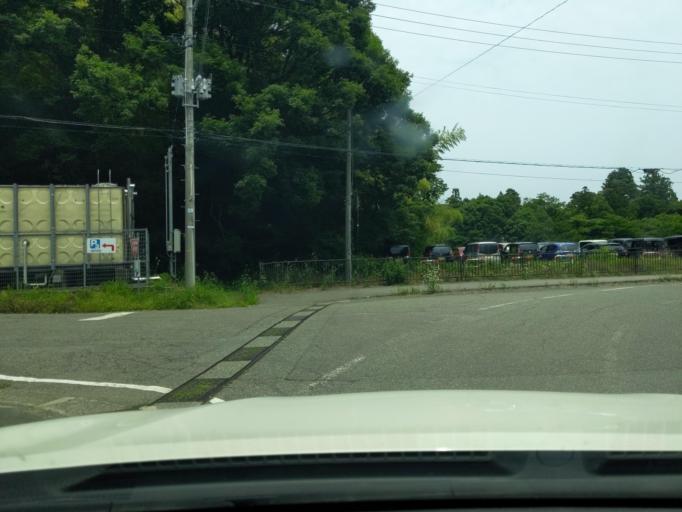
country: JP
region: Niigata
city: Kashiwazaki
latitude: 37.3583
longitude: 138.5392
